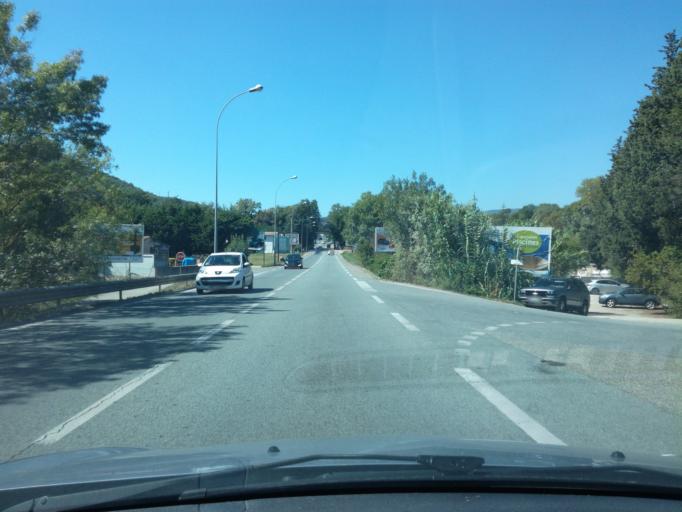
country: FR
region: Provence-Alpes-Cote d'Azur
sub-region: Departement du Var
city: Draguignan
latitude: 43.5207
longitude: 6.4704
